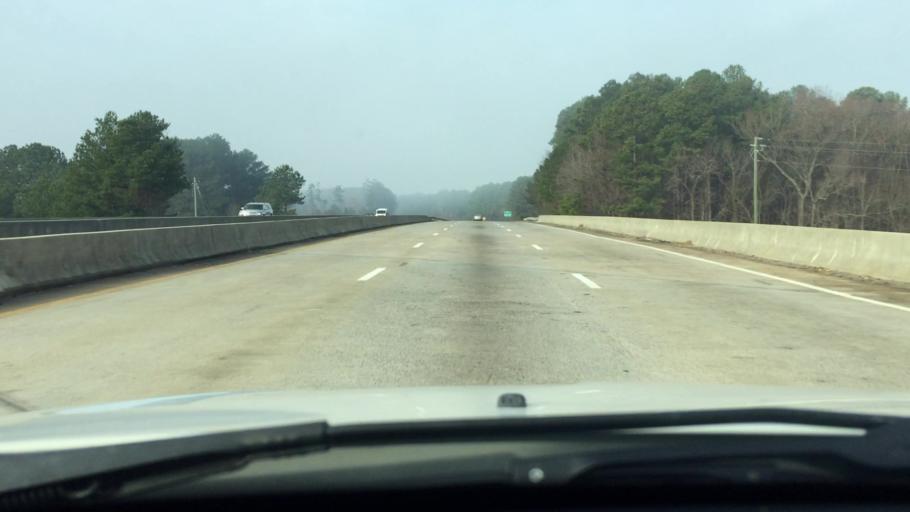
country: US
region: North Carolina
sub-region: Wake County
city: Holly Springs
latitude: 35.6441
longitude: -79.0020
